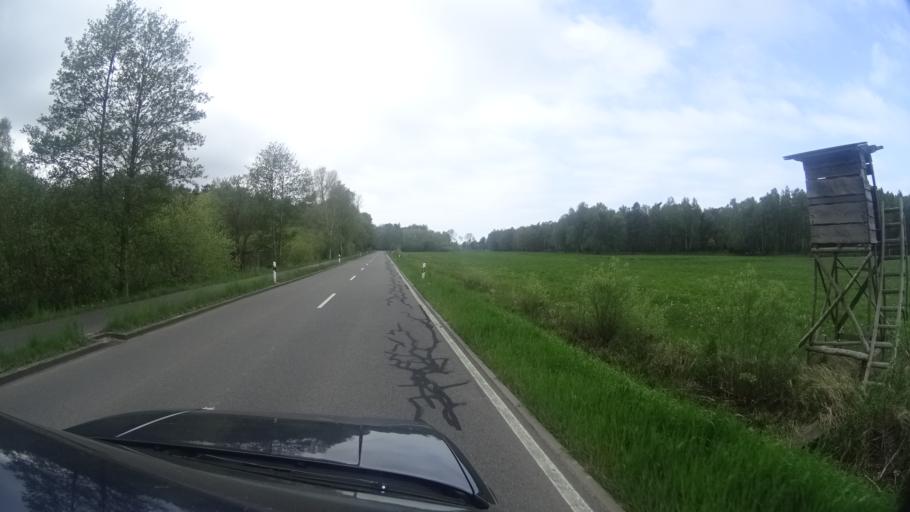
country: DE
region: Mecklenburg-Vorpommern
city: Ostseebad Dierhagen
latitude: 54.2709
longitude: 12.3409
